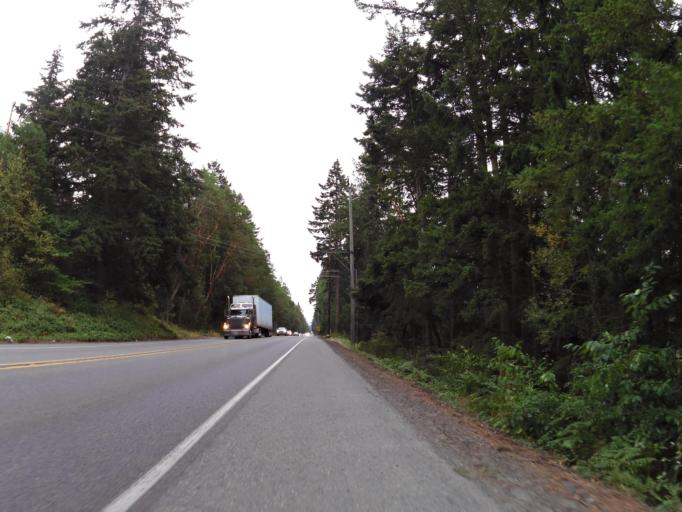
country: US
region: Washington
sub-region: Jefferson County
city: Port Hadlock-Irondale
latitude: 48.0678
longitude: -122.8150
